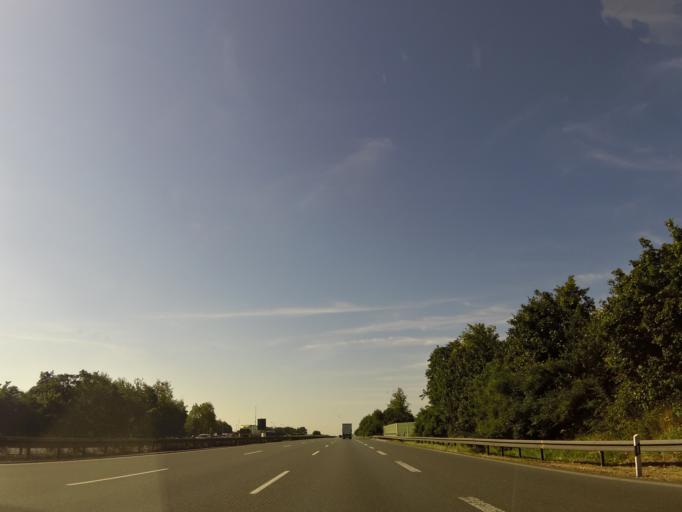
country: DE
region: Bavaria
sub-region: Regierungsbezirk Mittelfranken
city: Allersberg
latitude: 49.2248
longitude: 11.2239
